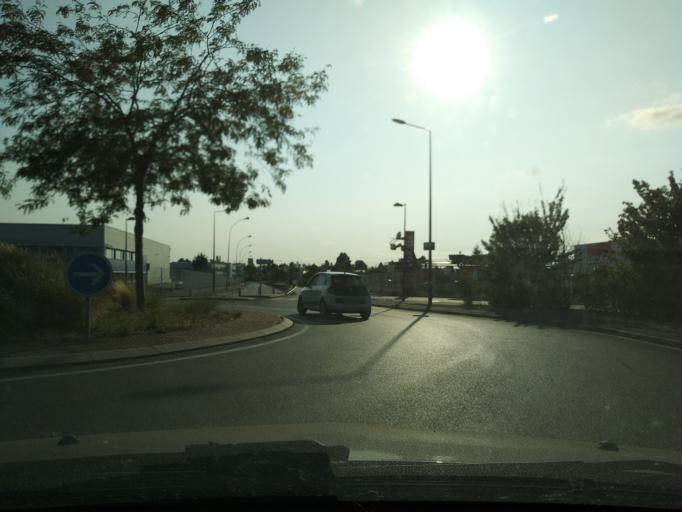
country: FR
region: Centre
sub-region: Departement d'Indre-et-Loire
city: Saint-Cyr-sur-Loire
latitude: 47.4316
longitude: 0.6904
